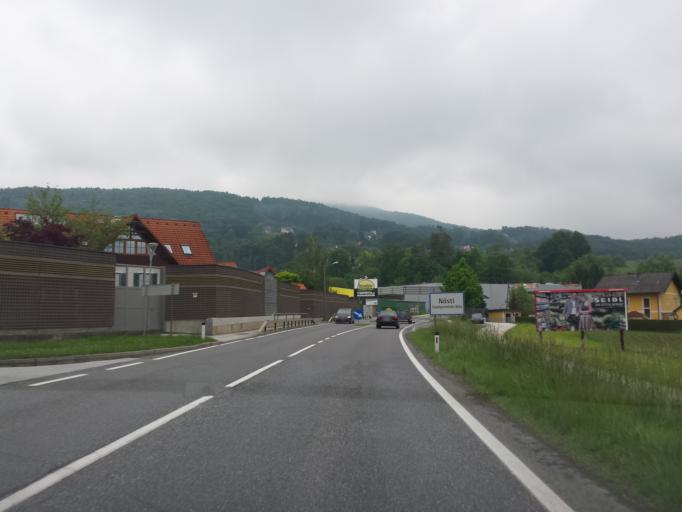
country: AT
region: Styria
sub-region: Politischer Bezirk Weiz
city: Unterfladnitz
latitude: 47.2225
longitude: 15.6674
